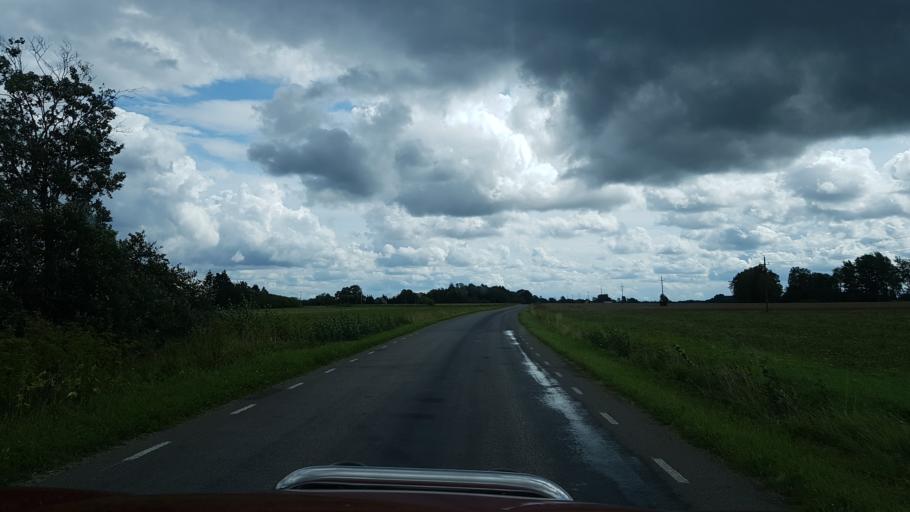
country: EE
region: Laeaene
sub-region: Lihula vald
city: Lihula
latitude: 58.7159
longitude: 23.9946
